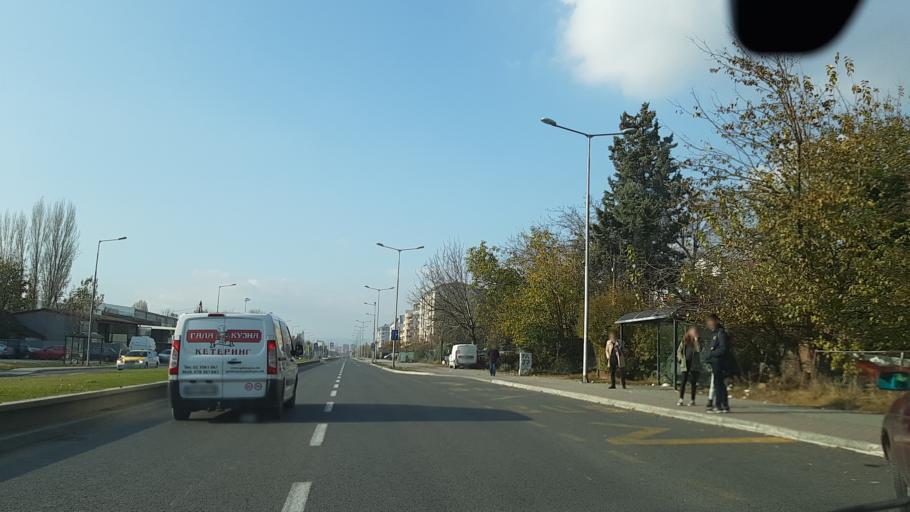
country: MK
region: Kisela Voda
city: Usje
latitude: 41.9787
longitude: 21.4617
